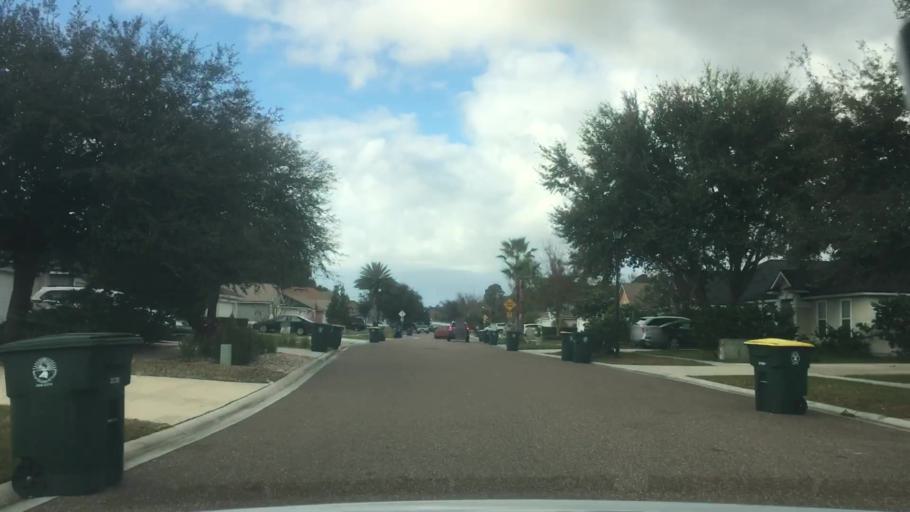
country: US
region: Florida
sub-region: Duval County
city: Neptune Beach
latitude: 30.3033
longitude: -81.5031
